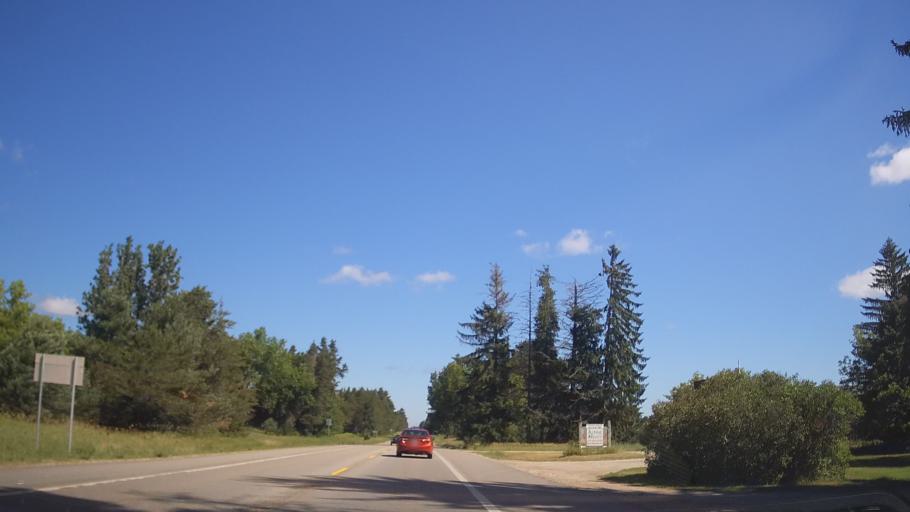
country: US
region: Michigan
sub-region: Cheboygan County
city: Indian River
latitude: 45.4961
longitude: -84.7812
